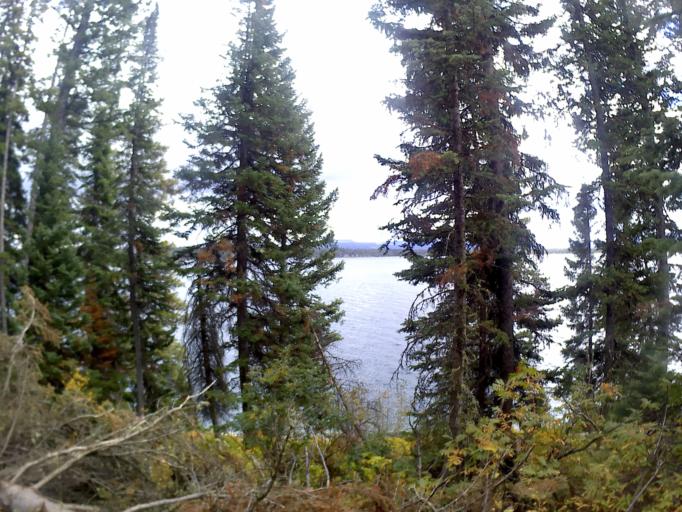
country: US
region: Wyoming
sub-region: Teton County
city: Moose Wilson Road
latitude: 43.7715
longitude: -110.7397
